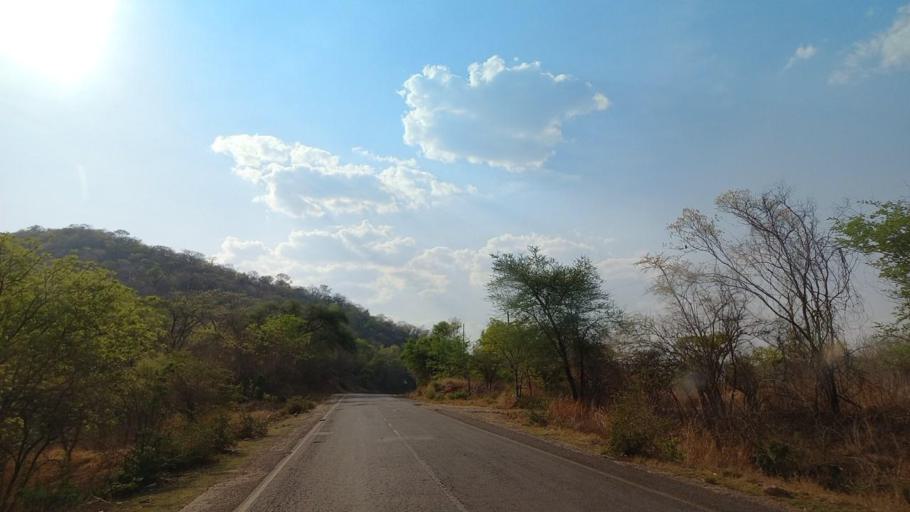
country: ZM
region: Lusaka
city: Luangwa
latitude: -14.9851
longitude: 30.1870
